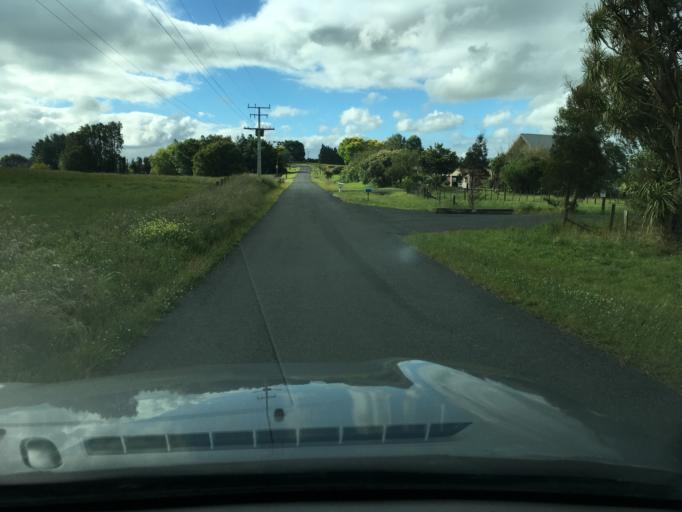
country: NZ
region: Waikato
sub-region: Hamilton City
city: Hamilton
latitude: -37.8274
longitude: 175.1792
